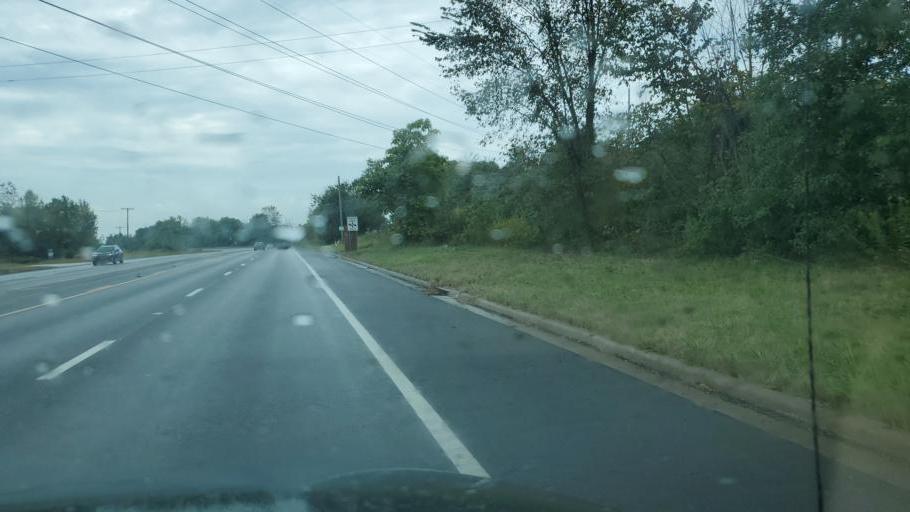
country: US
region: Ohio
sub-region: Licking County
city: Hebron
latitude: 39.9888
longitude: -82.4820
